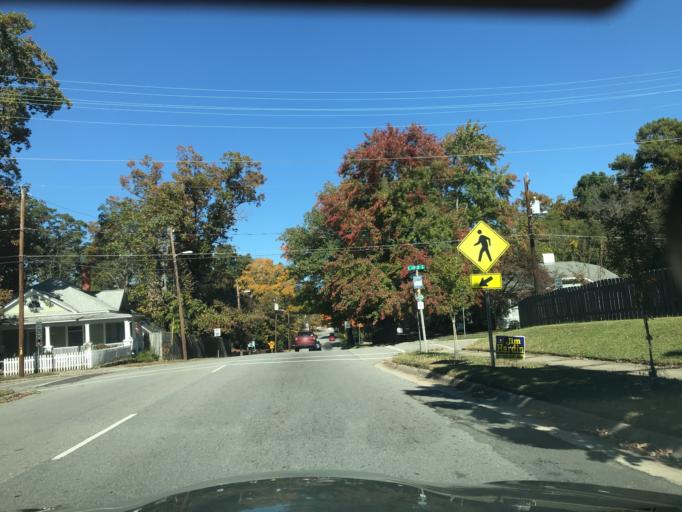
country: US
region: North Carolina
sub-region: Durham County
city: Durham
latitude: 36.0069
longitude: -78.8924
